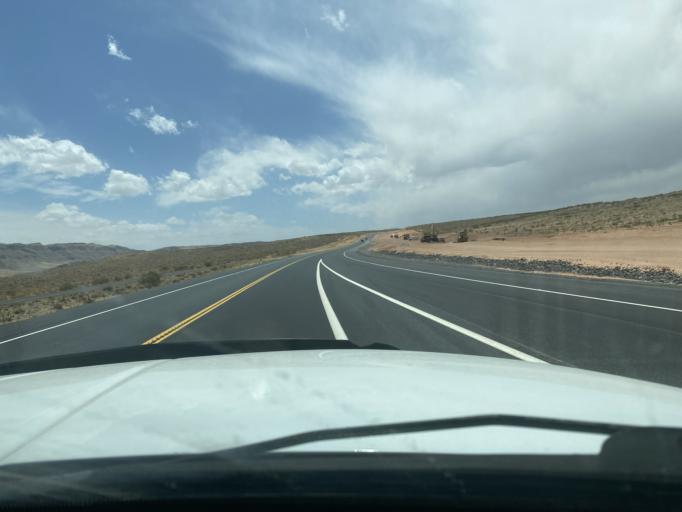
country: US
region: Utah
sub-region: Washington County
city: Hurricane
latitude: 37.1212
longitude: -113.3433
